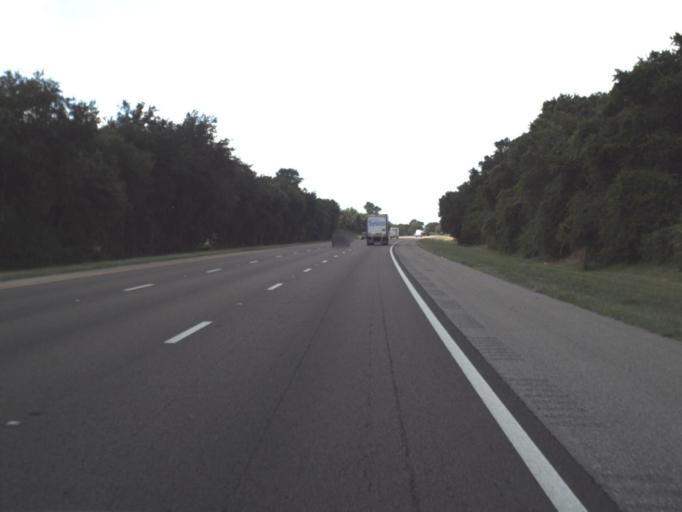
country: US
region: Florida
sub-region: Hillsborough County
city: Apollo Beach
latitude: 27.7692
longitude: -82.3646
